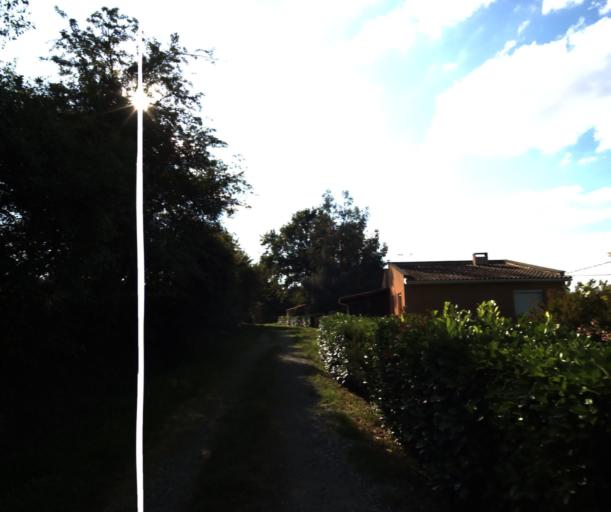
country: FR
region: Midi-Pyrenees
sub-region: Departement de la Haute-Garonne
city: Labastidette
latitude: 43.4691
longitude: 1.2083
